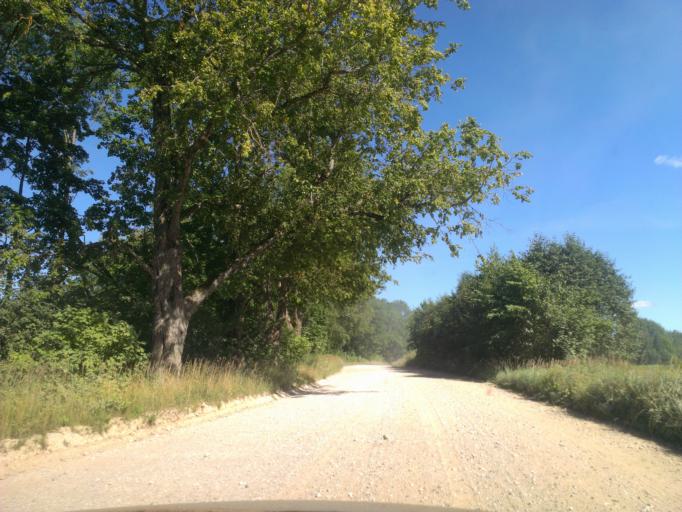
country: LV
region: Malpils
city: Malpils
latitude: 57.0594
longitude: 25.1553
